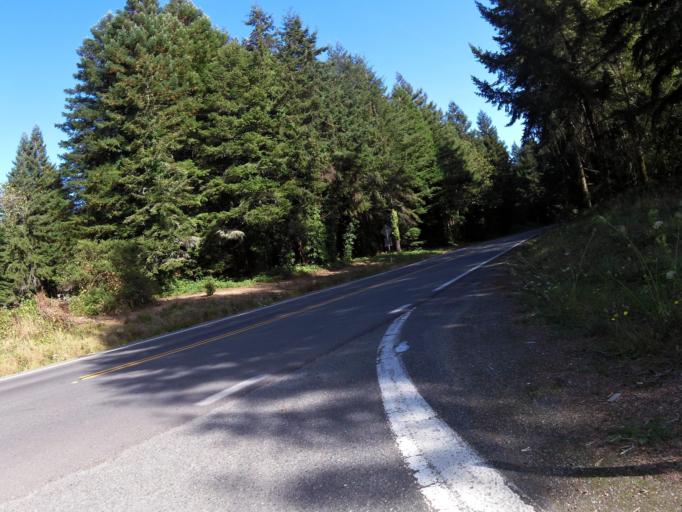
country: US
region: California
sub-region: Del Norte County
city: Bertsch-Oceanview
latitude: 41.8409
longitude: -124.1108
